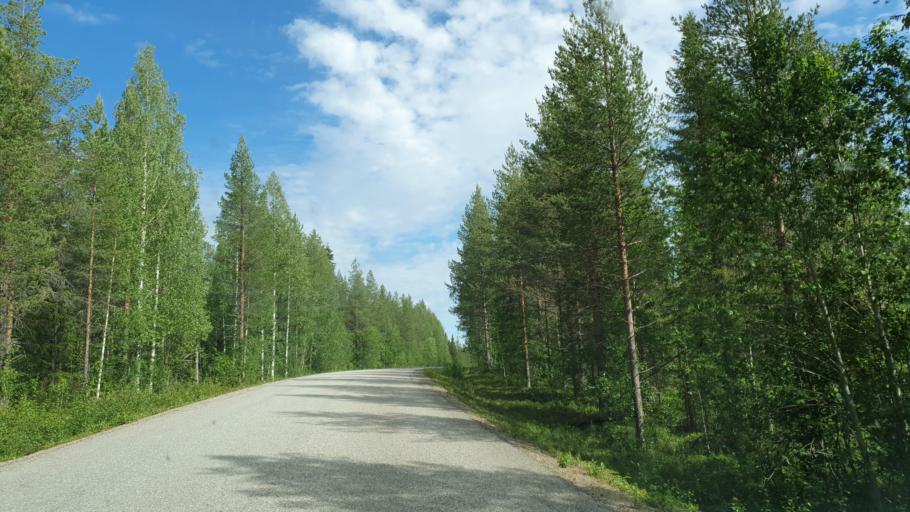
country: FI
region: Kainuu
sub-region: Kehys-Kainuu
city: Kuhmo
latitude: 64.5379
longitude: 29.3132
